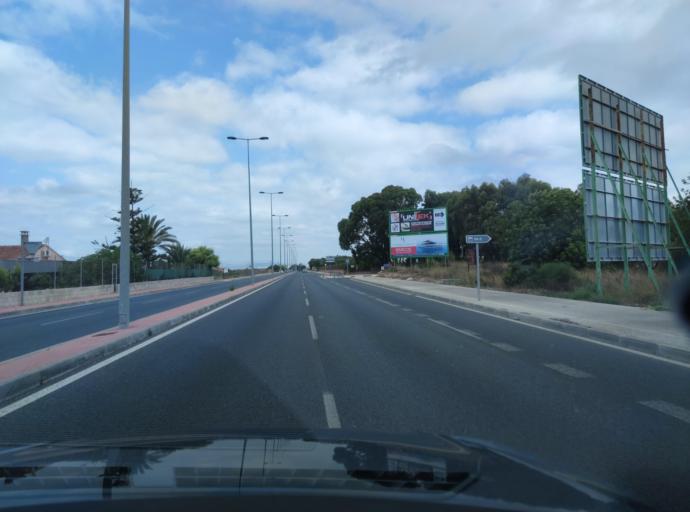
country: ES
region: Valencia
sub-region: Provincia de Alicante
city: Santa Pola
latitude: 38.2061
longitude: -0.5813
